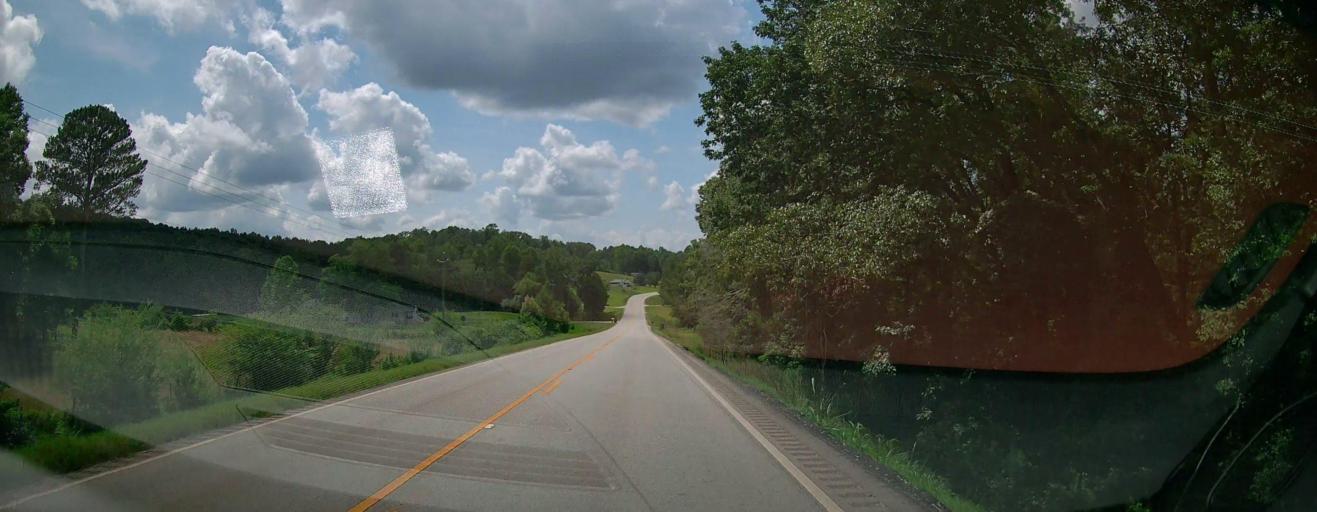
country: US
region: Georgia
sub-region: Carroll County
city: Bowdon
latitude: 33.5466
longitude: -85.4012
